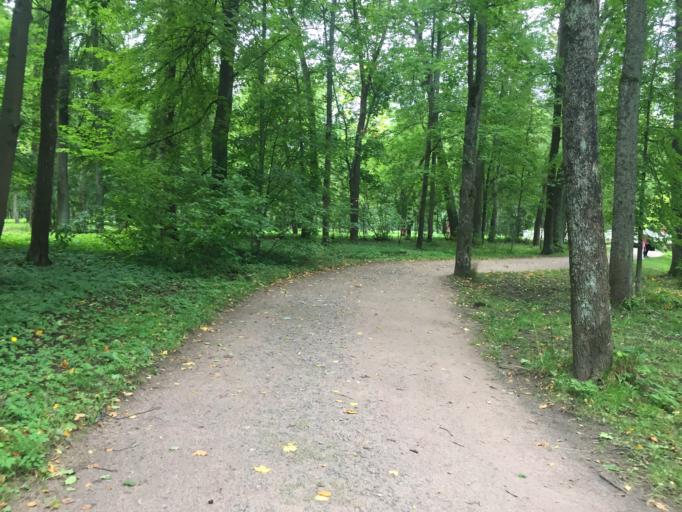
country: RU
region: St.-Petersburg
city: Pushkin
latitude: 59.7208
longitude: 30.3893
